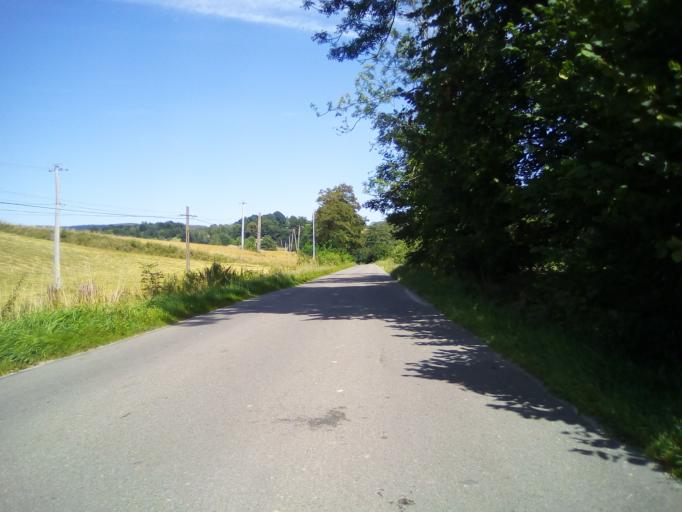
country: PL
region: Subcarpathian Voivodeship
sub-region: Powiat strzyzowski
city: Konieczkowa
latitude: 49.8296
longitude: 21.9290
